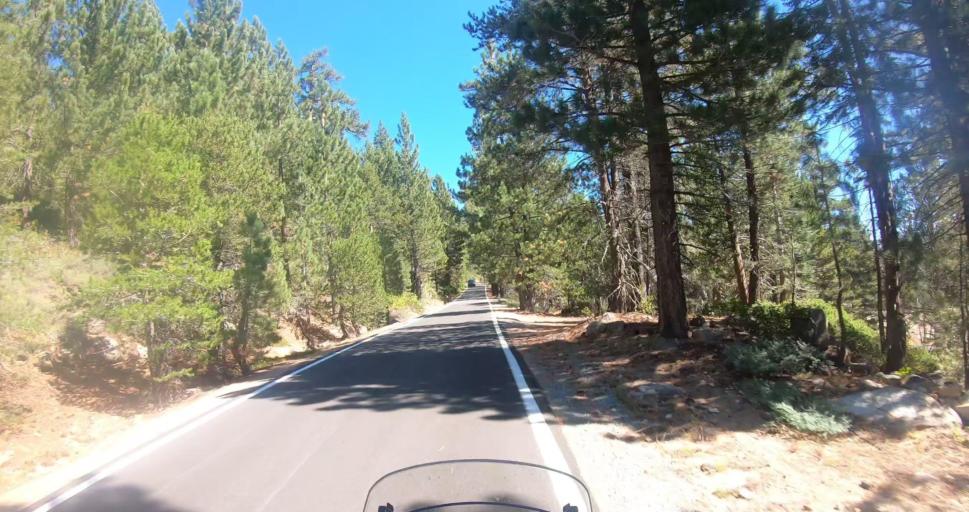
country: US
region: Nevada
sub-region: Douglas County
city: Gardnerville Ranchos
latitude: 38.5470
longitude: -119.8674
